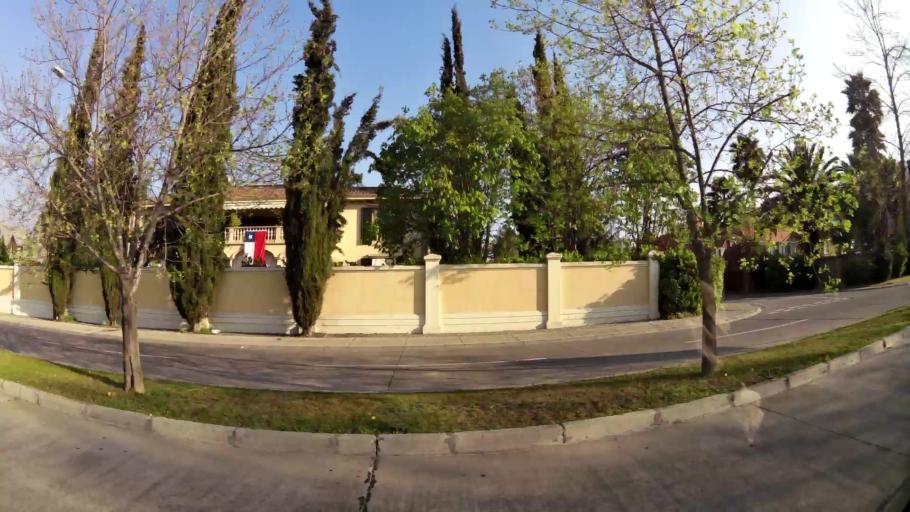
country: CL
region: Santiago Metropolitan
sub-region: Provincia de Santiago
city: Villa Presidente Frei, Nunoa, Santiago, Chile
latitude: -33.3504
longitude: -70.5394
